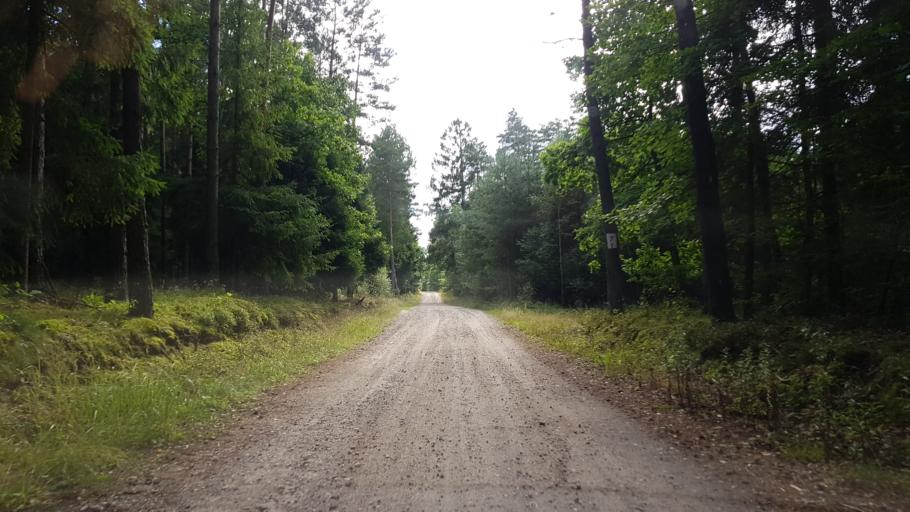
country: PL
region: West Pomeranian Voivodeship
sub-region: Powiat bialogardzki
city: Tychowo
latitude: 54.0045
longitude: 16.3030
